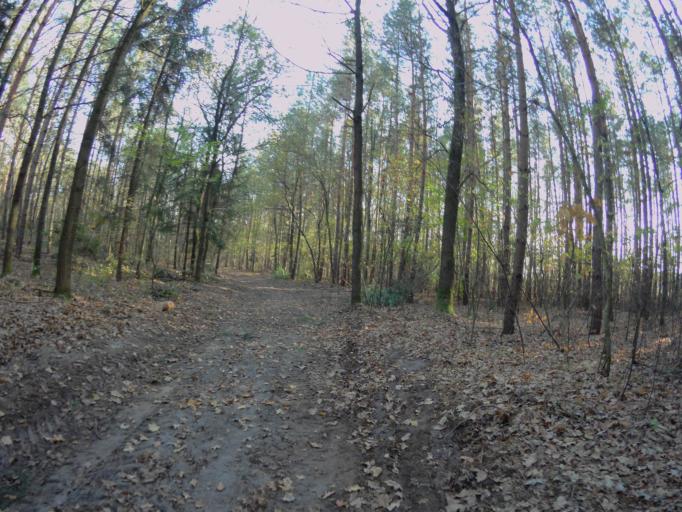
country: PL
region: Subcarpathian Voivodeship
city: Nowa Sarzyna
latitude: 50.3058
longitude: 22.3542
